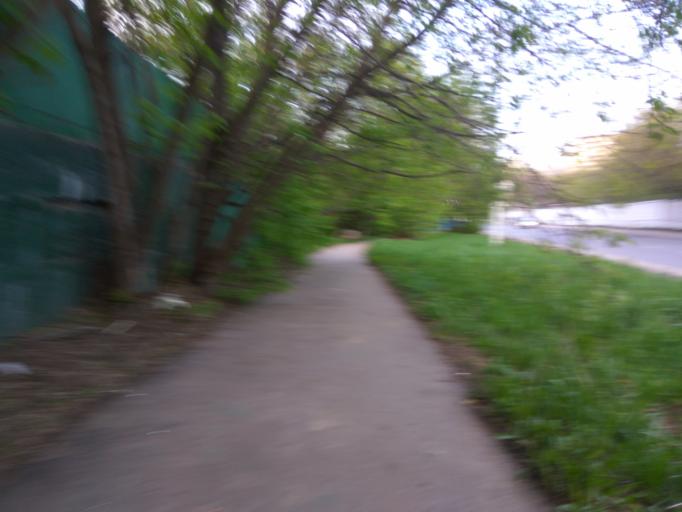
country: RU
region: Moscow
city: Kotlovka
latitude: 55.6843
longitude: 37.6052
